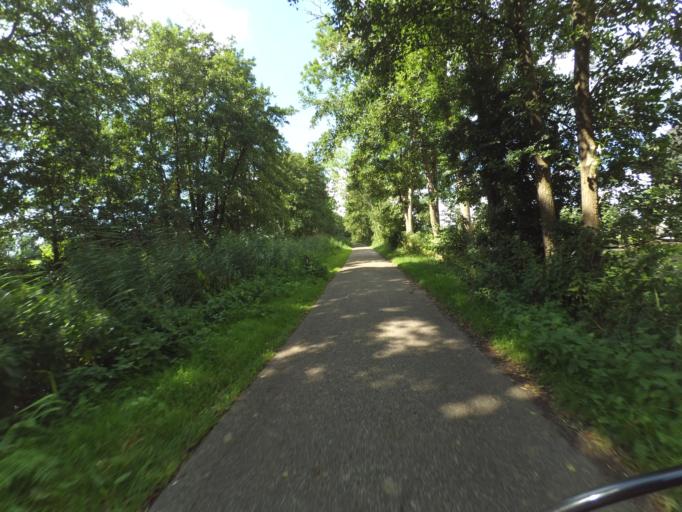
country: NL
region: Friesland
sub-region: Gemeente Achtkarspelen
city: Twijzelerheide
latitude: 53.2116
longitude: 6.0571
